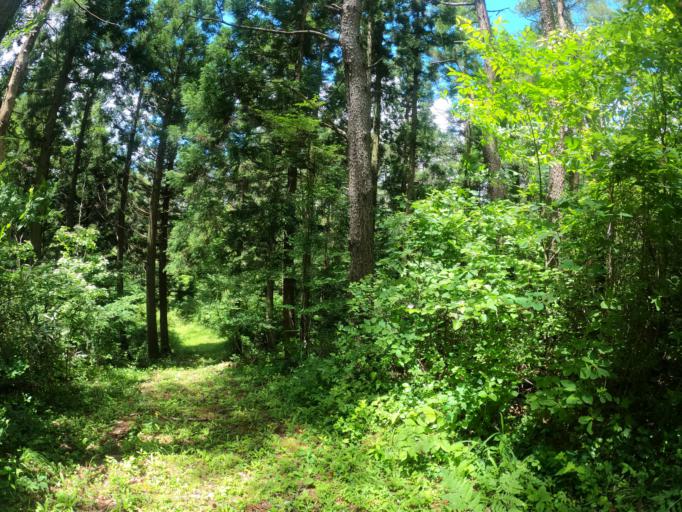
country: JP
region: Miyagi
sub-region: Oshika Gun
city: Onagawa Cho
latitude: 38.6892
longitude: 141.3590
